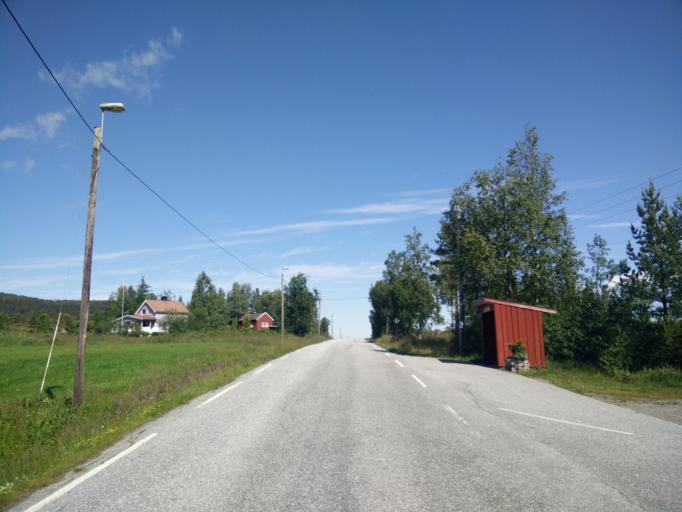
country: NO
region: More og Romsdal
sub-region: Kristiansund
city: Rensvik
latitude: 63.0625
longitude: 7.8688
